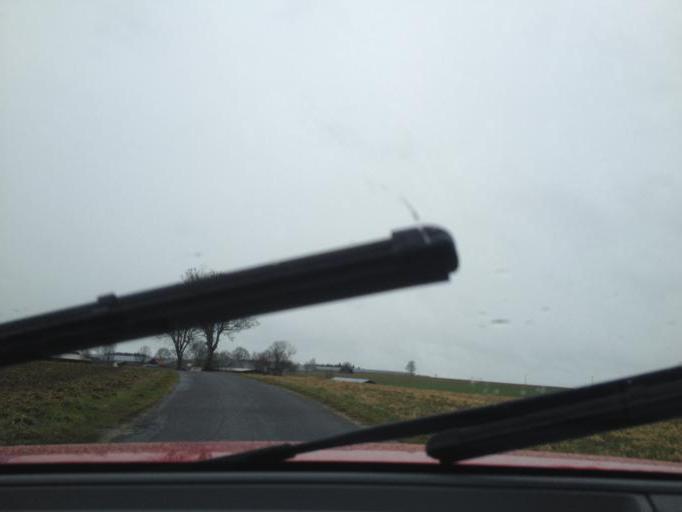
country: DE
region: Bavaria
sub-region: Upper Franconia
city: Thiersheim
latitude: 50.0856
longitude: 12.1393
